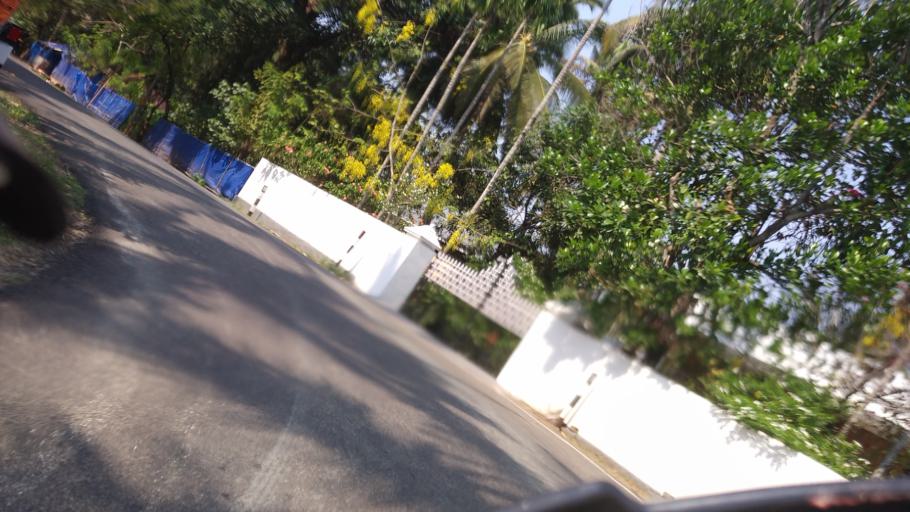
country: IN
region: Kerala
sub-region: Thrissur District
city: Thanniyam
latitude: 10.3686
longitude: 76.1059
